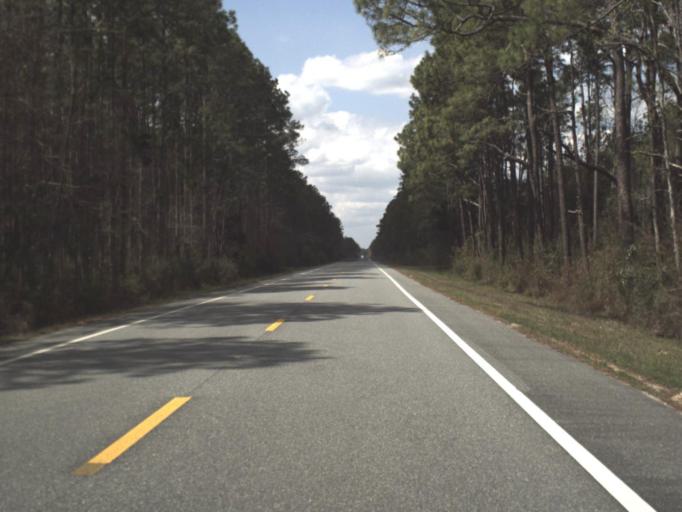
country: US
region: Florida
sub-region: Franklin County
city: Apalachicola
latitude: 29.8404
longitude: -84.9445
